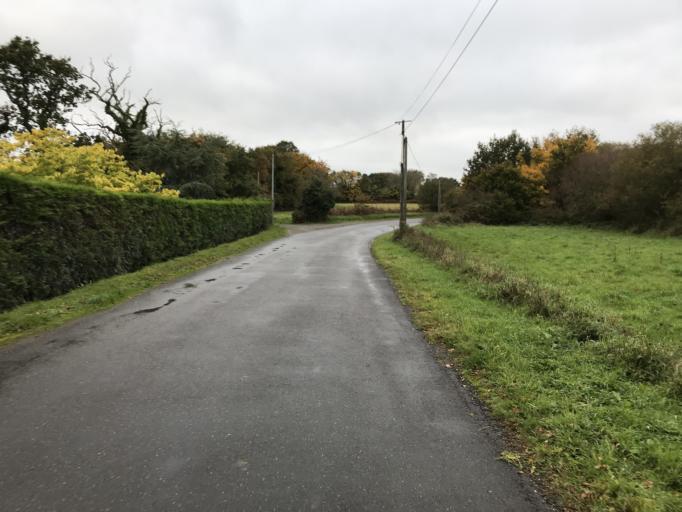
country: FR
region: Brittany
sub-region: Departement du Finistere
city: Logonna-Daoulas
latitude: 48.3342
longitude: -4.3080
